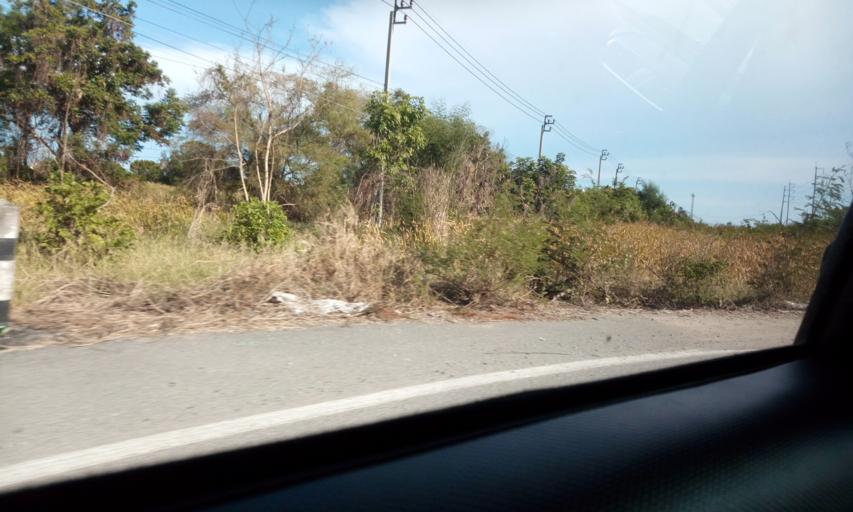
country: TH
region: Samut Prakan
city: Bang Bo District
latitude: 13.5303
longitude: 100.7503
